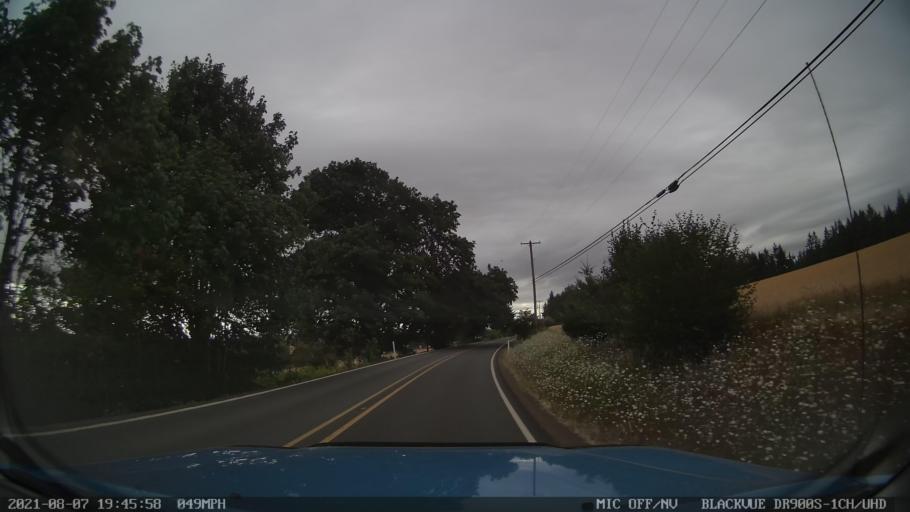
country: US
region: Oregon
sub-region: Marion County
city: Silverton
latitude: 44.9533
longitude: -122.7004
